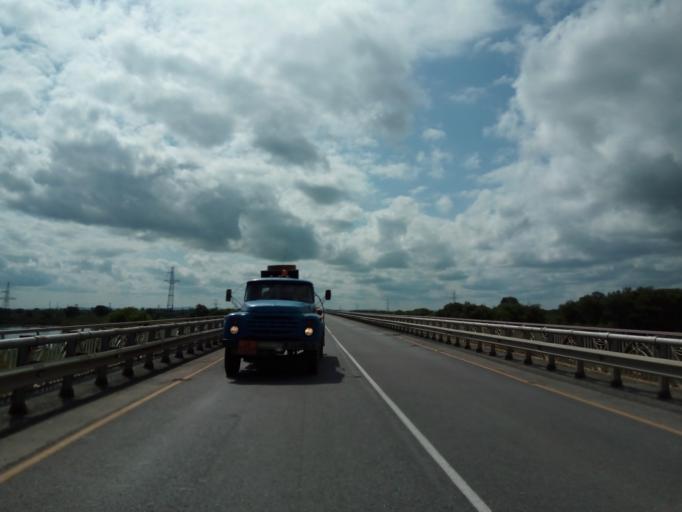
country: RU
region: Primorskiy
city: Dal'nerechensk
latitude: 45.9645
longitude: 133.7831
